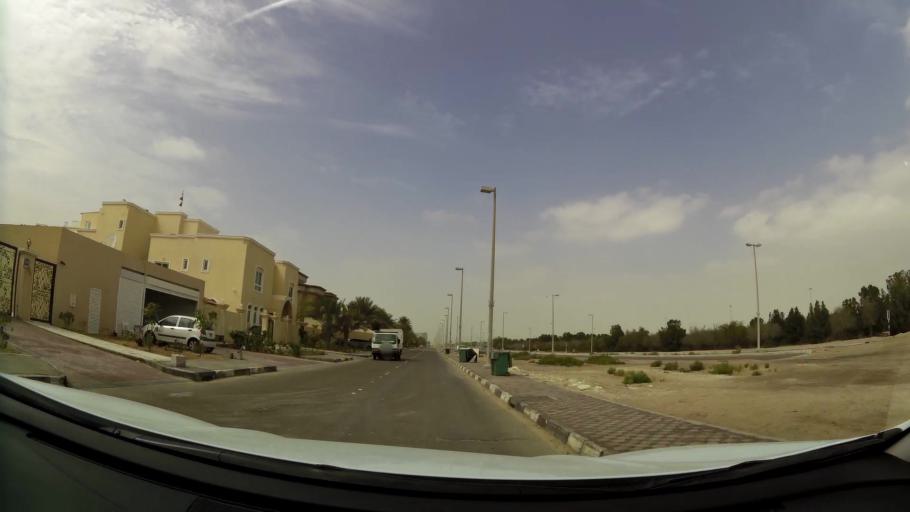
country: AE
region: Abu Dhabi
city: Abu Dhabi
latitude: 24.3936
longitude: 54.5136
